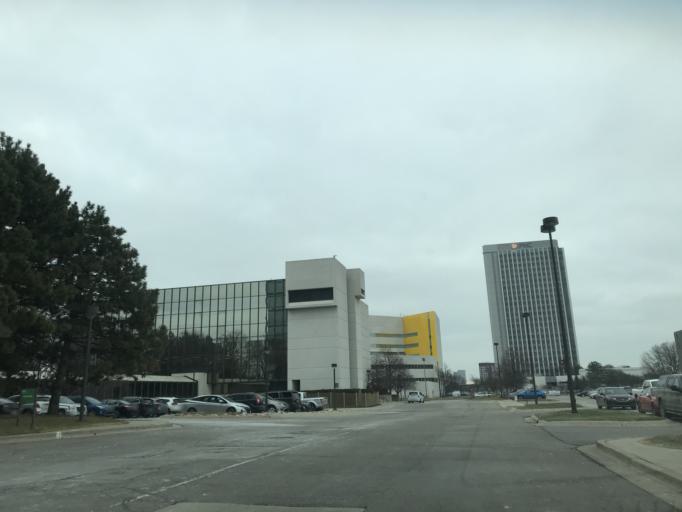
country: US
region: Michigan
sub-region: Oakland County
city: Clawson
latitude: 42.5605
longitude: -83.1661
